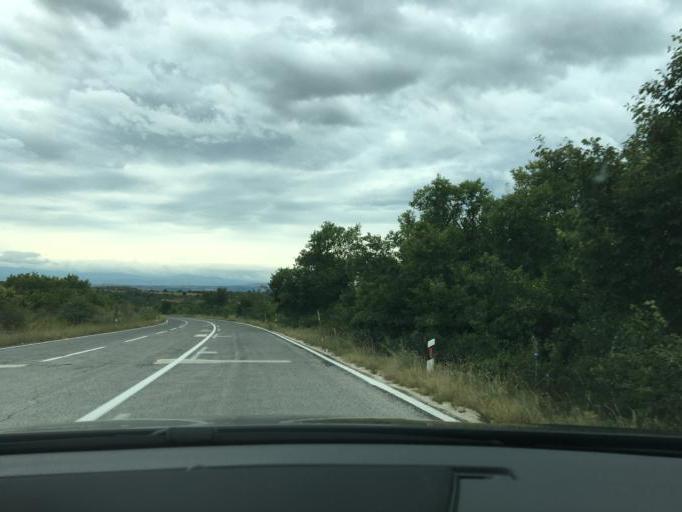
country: MK
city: Klechovce
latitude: 42.1507
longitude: 21.9615
